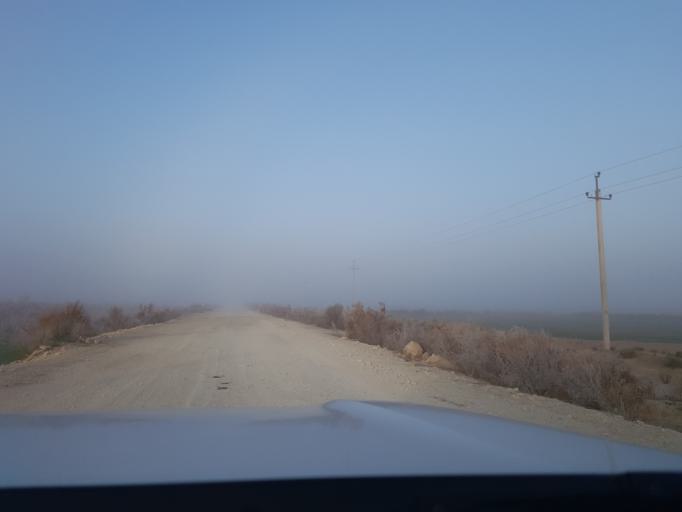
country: TM
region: Dasoguz
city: Koeneuergench
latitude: 41.8454
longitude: 58.4260
